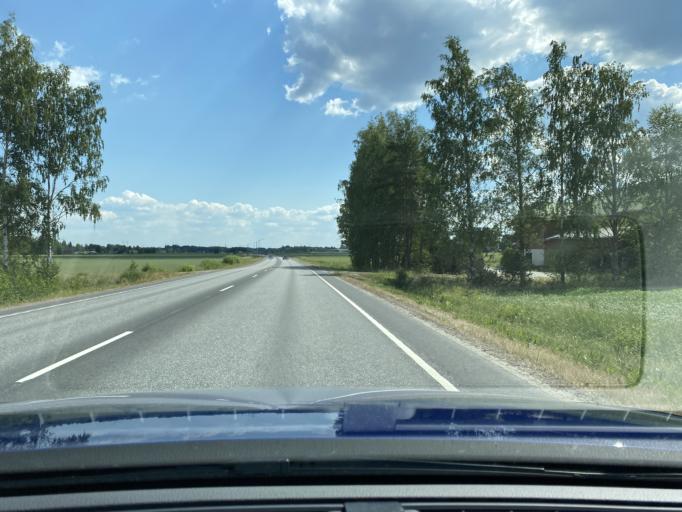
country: FI
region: Satakunta
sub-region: Rauma
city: Eura
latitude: 61.1496
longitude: 22.1001
